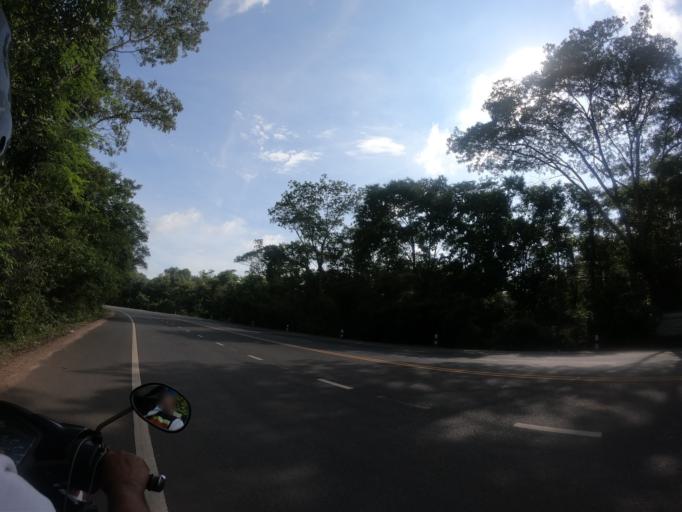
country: TH
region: Surin
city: Kap Choeng
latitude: 14.4475
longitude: 103.7006
